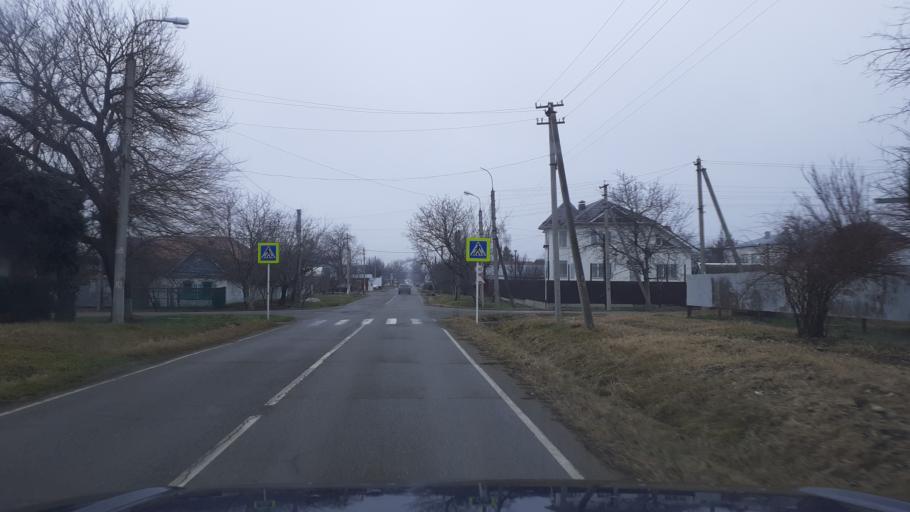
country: RU
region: Adygeya
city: Maykop
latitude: 44.6186
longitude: 40.0816
